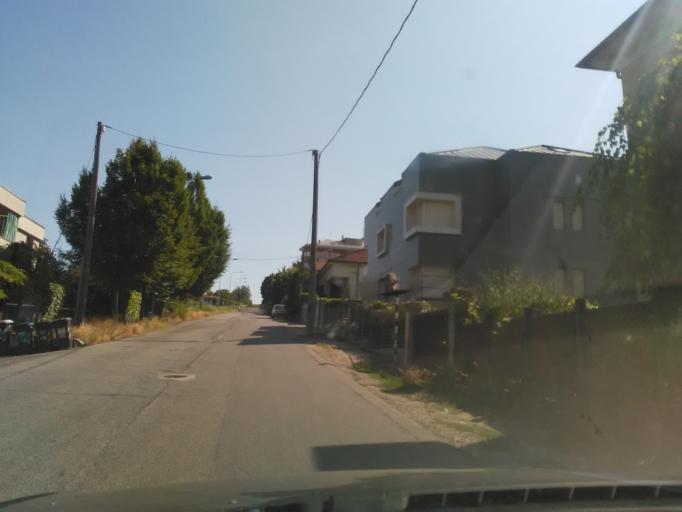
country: IT
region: Piedmont
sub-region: Provincia di Alessandria
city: Casale Monferrato
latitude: 45.1298
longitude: 8.4423
